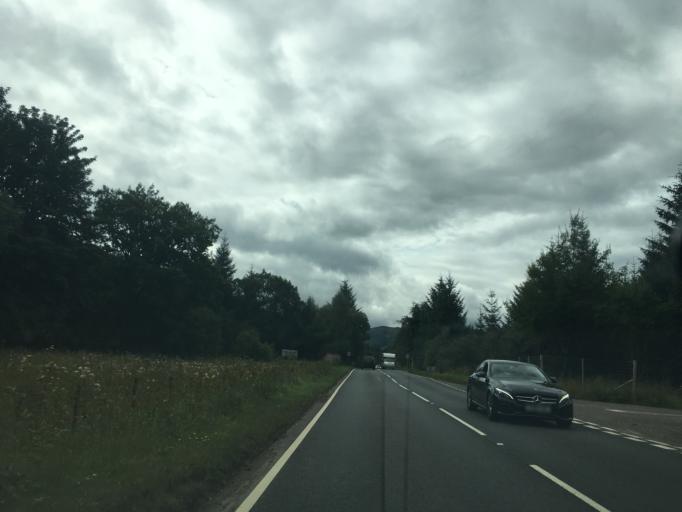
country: GB
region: Scotland
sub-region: Stirling
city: Callander
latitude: 56.3636
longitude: -4.3032
